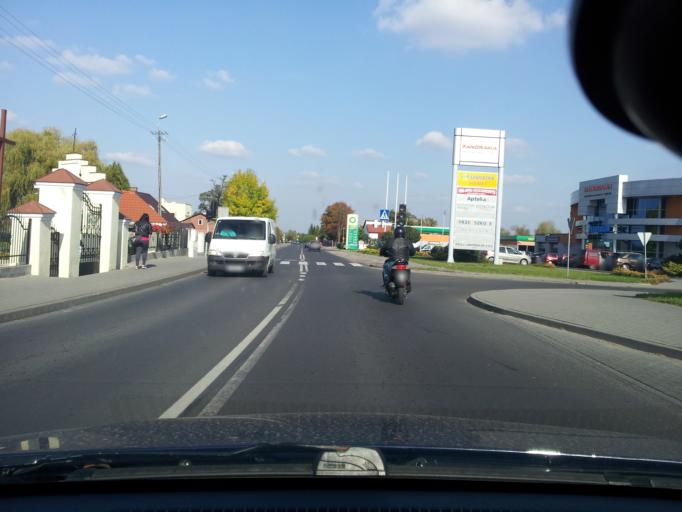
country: PL
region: Kujawsko-Pomorskie
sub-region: Powiat wloclawski
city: Fabianki
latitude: 52.6827
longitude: 19.0984
